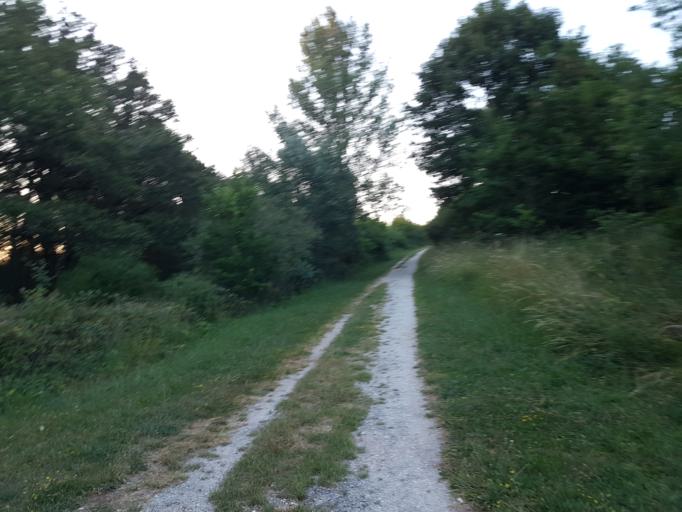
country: FR
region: Centre
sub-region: Departement d'Indre-et-Loire
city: Saint-Avertin
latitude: 47.3501
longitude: 0.7615
